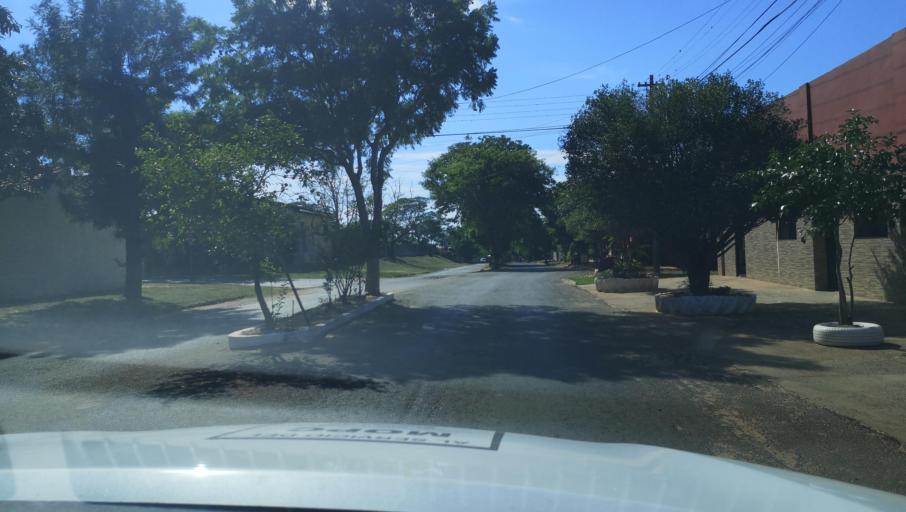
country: PY
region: Misiones
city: Santa Maria
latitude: -26.8939
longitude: -57.0246
